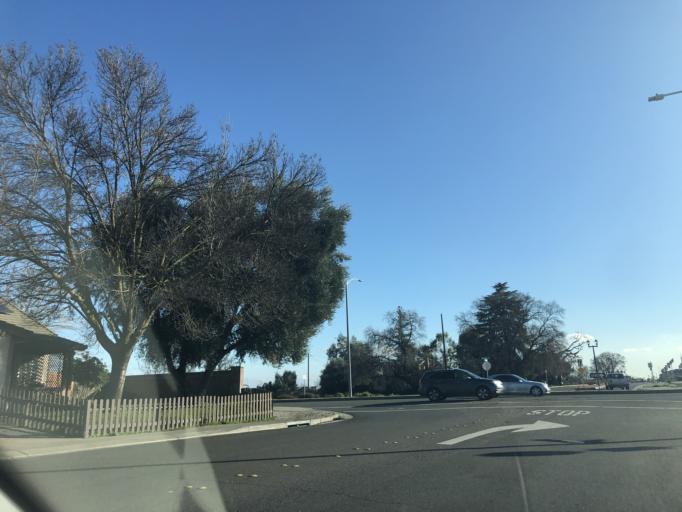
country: US
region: California
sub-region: Yolo County
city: Woodland
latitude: 38.6630
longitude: -121.7472
